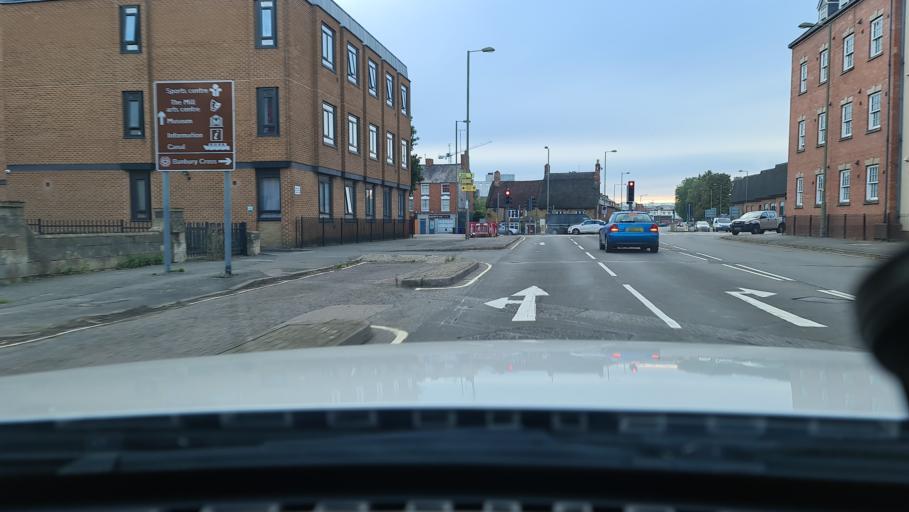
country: GB
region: England
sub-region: Oxfordshire
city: Banbury
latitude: 52.0636
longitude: -1.3408
